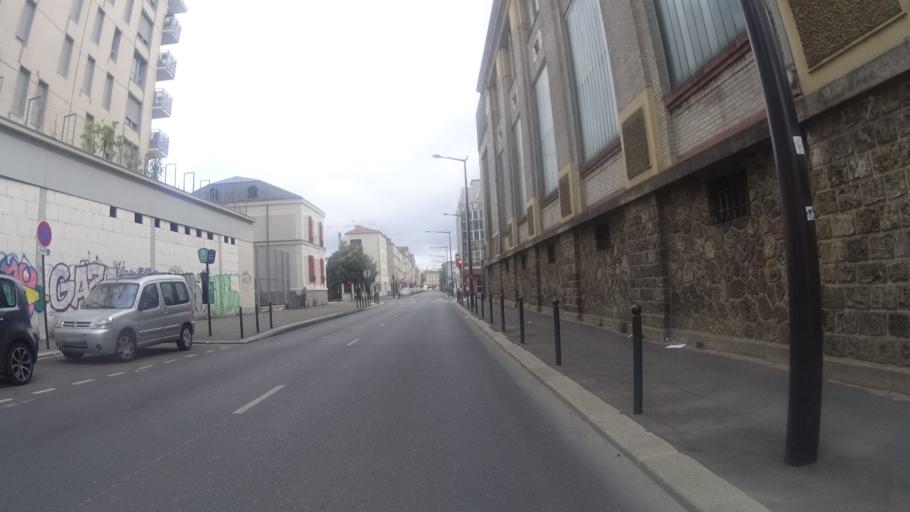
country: FR
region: Ile-de-France
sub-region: Departement du Val-de-Marne
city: Charenton-le-Pont
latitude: 48.8110
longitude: 2.4032
